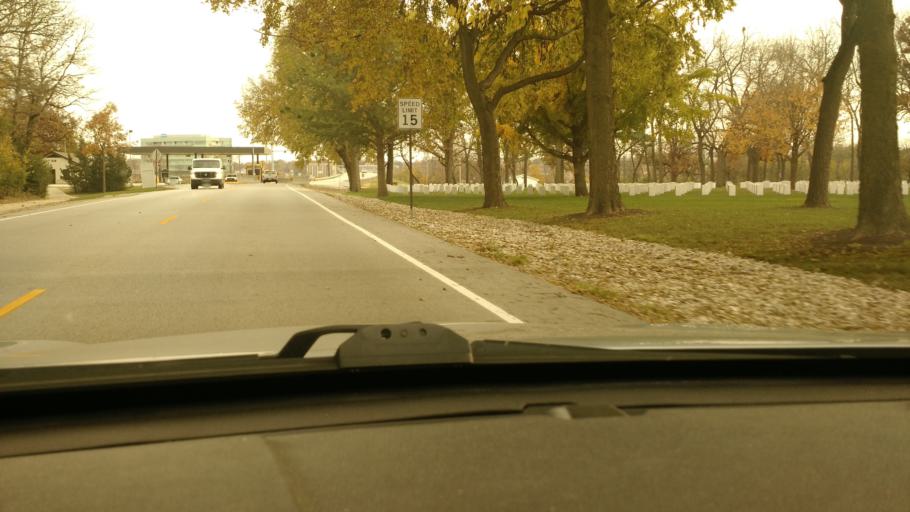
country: US
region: Illinois
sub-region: Rock Island County
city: Moline
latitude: 41.5142
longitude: -90.5223
